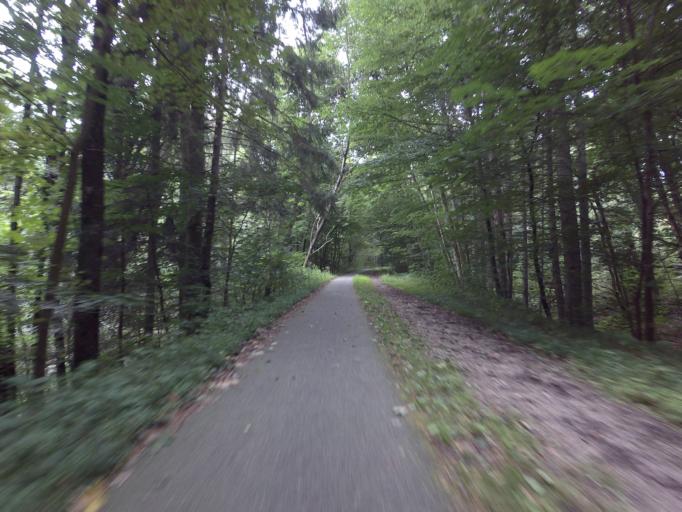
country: DK
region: Central Jutland
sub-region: Silkeborg Kommune
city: Virklund
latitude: 56.1184
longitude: 9.5721
